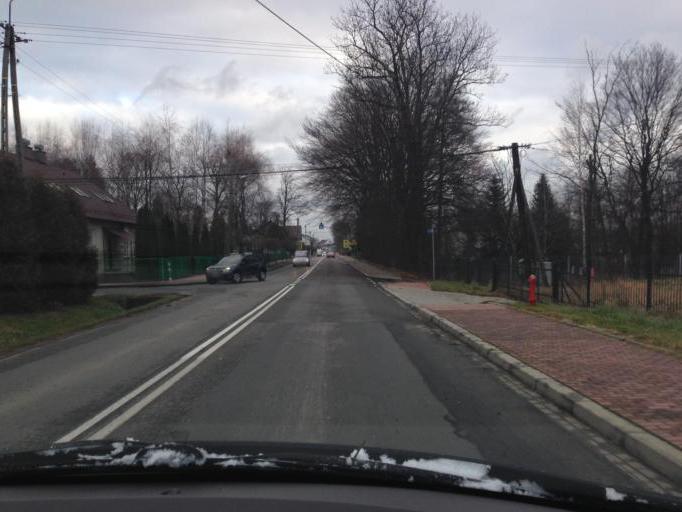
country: PL
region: Lesser Poland Voivodeship
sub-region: Powiat wielicki
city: Gdow
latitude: 49.9082
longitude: 20.1915
